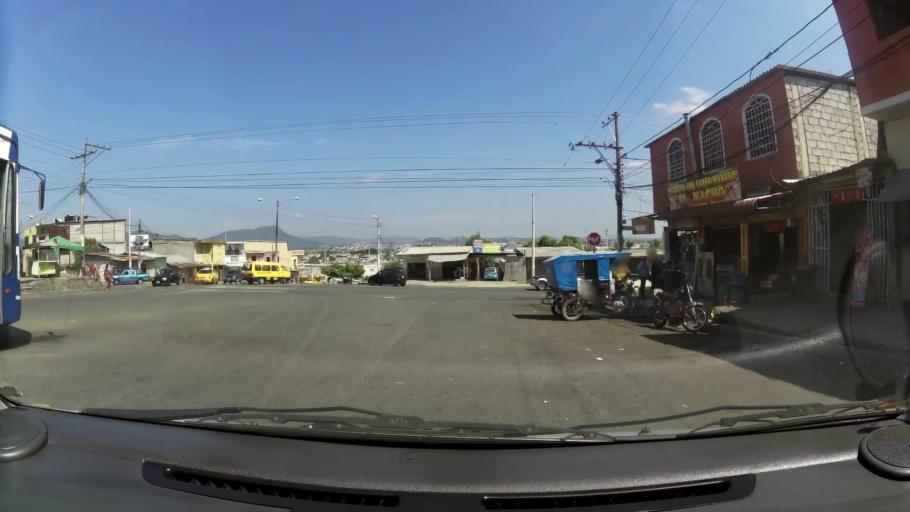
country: EC
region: Guayas
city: Eloy Alfaro
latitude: -2.1260
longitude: -79.9181
